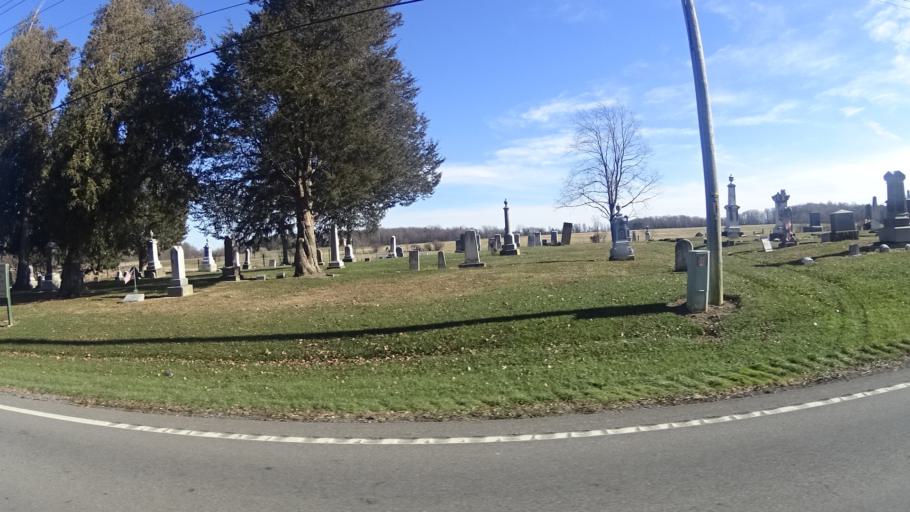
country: US
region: Ohio
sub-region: Lorain County
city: Camden
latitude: 41.2796
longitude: -82.3016
